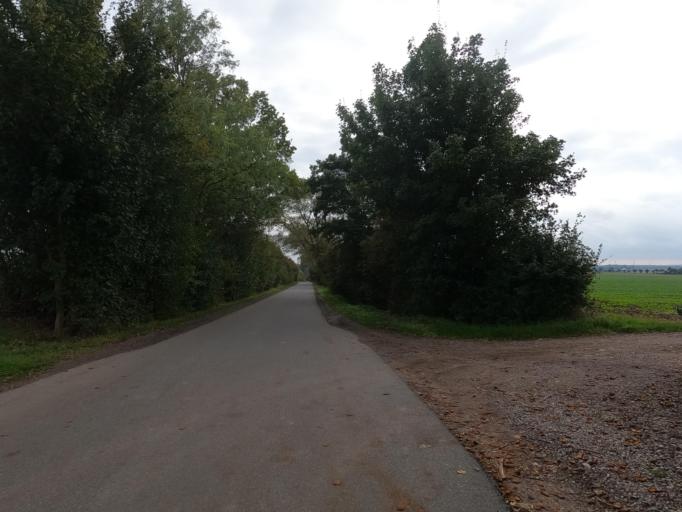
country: DE
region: Schleswig-Holstein
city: Neukirchen
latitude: 54.3500
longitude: 11.0339
